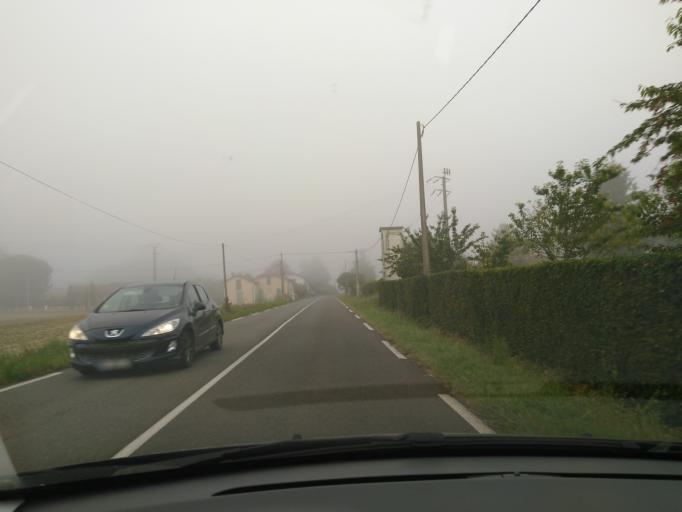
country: FR
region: Aquitaine
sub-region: Departement des Landes
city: Villeneuve-de-Marsan
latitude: 43.8867
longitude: -0.3285
